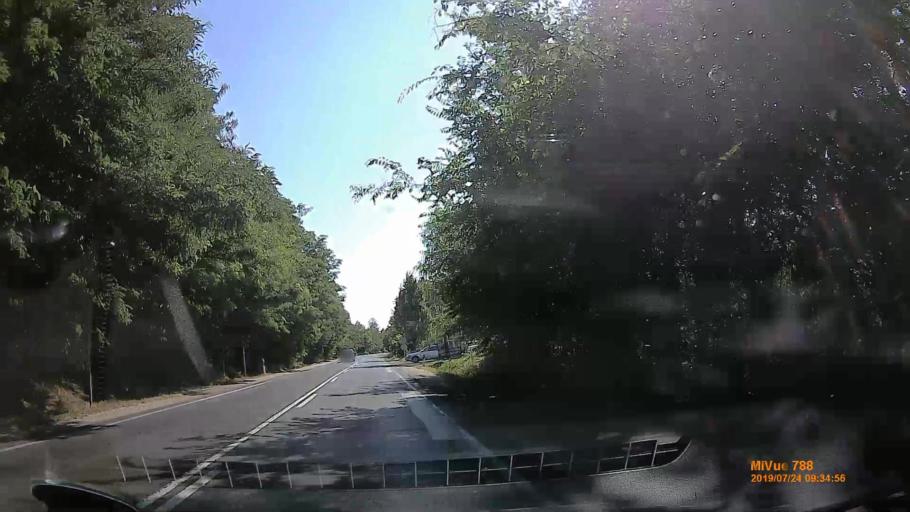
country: HU
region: Szabolcs-Szatmar-Bereg
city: Napkor
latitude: 47.9546
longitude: 21.8763
